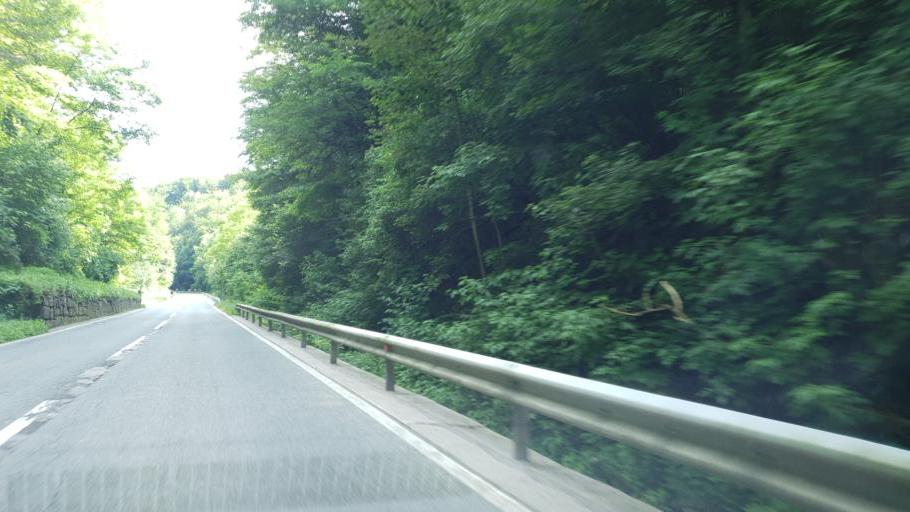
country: SI
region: Ilirska Bistrica
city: Ilirska Bistrica
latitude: 45.5186
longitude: 14.2519
